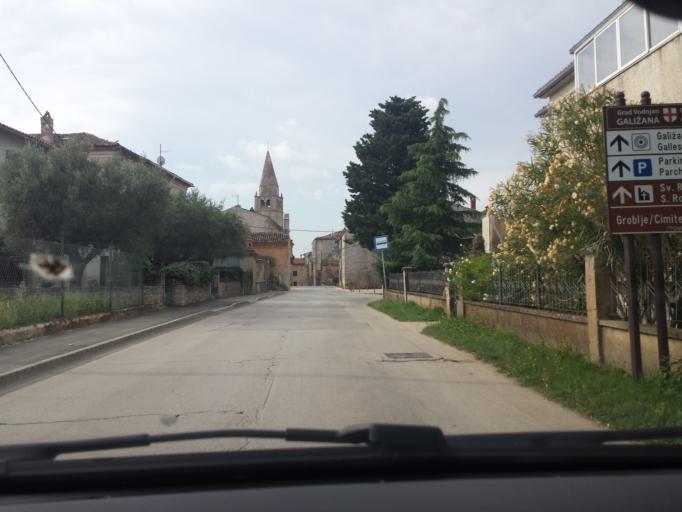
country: HR
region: Istarska
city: Galizana
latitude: 44.9352
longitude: 13.8701
